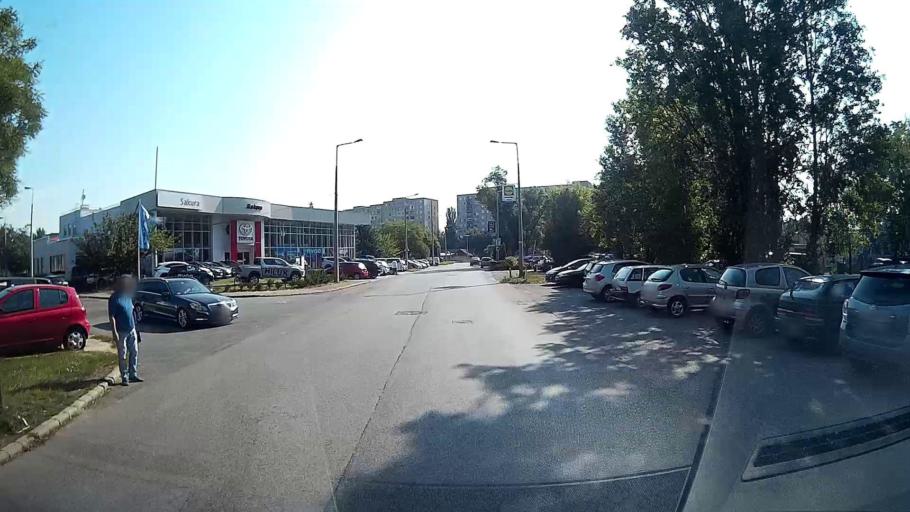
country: HU
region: Budapest
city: Budapest III. keruelet
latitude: 47.5558
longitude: 19.0391
